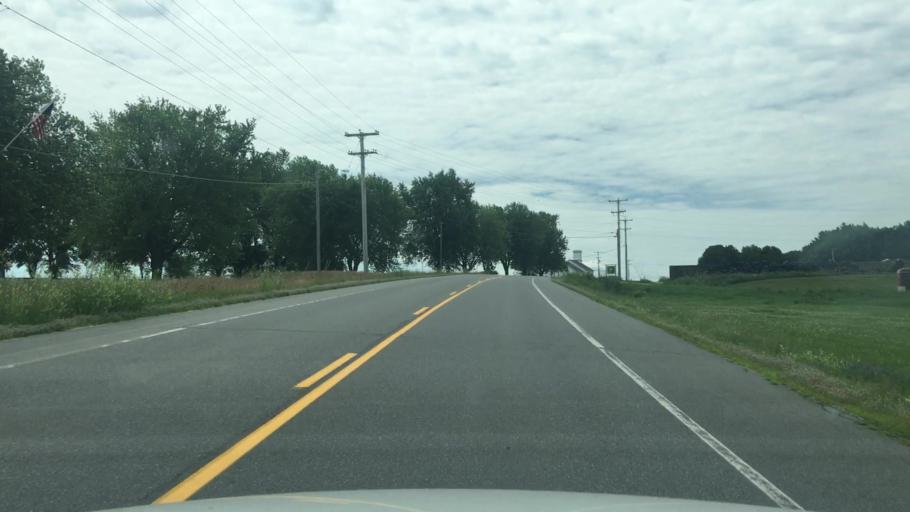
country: US
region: Maine
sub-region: Waldo County
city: Troy
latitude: 44.5428
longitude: -69.2653
